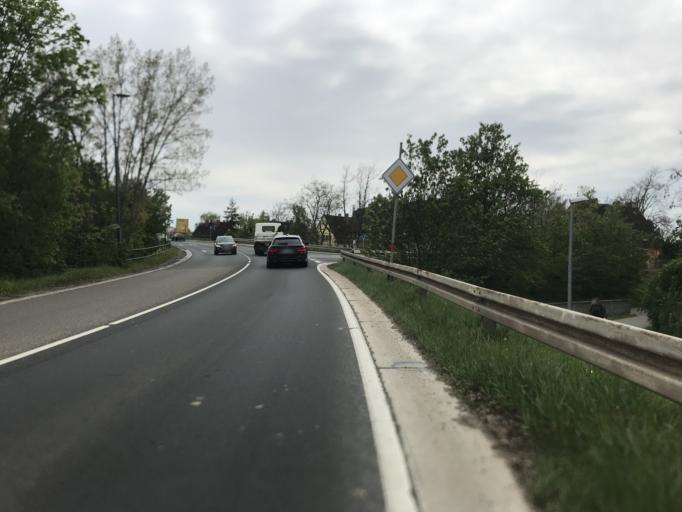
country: DE
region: Rheinland-Pfalz
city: Gau-Algesheim
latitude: 49.9622
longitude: 8.0137
